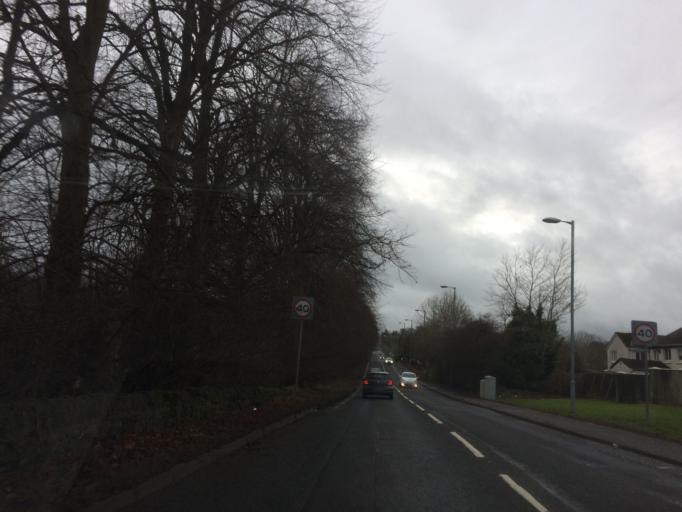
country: GB
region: Scotland
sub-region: East Renfrewshire
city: Newton Mearns
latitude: 55.7980
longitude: -4.3261
